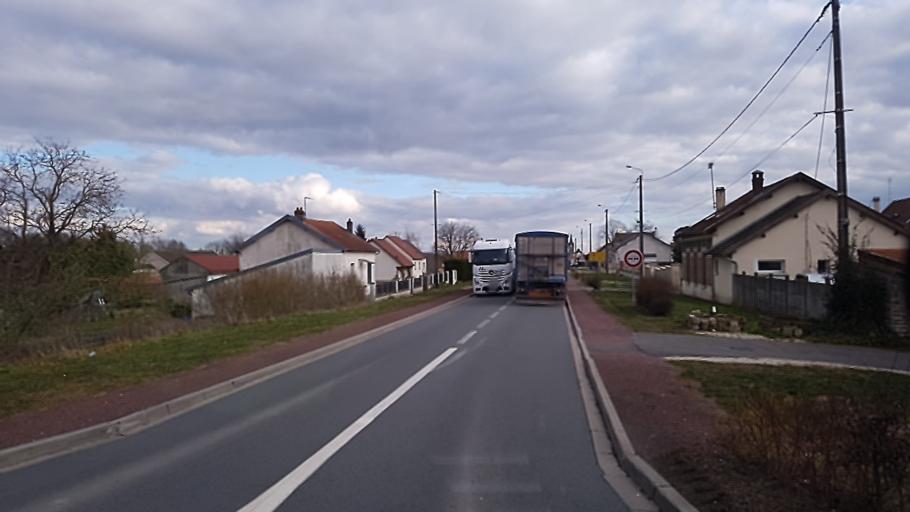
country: FR
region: Picardie
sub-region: Departement de l'Aisne
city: Saint-Erme-Outre-et-Ramecourt
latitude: 49.4675
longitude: 3.8177
